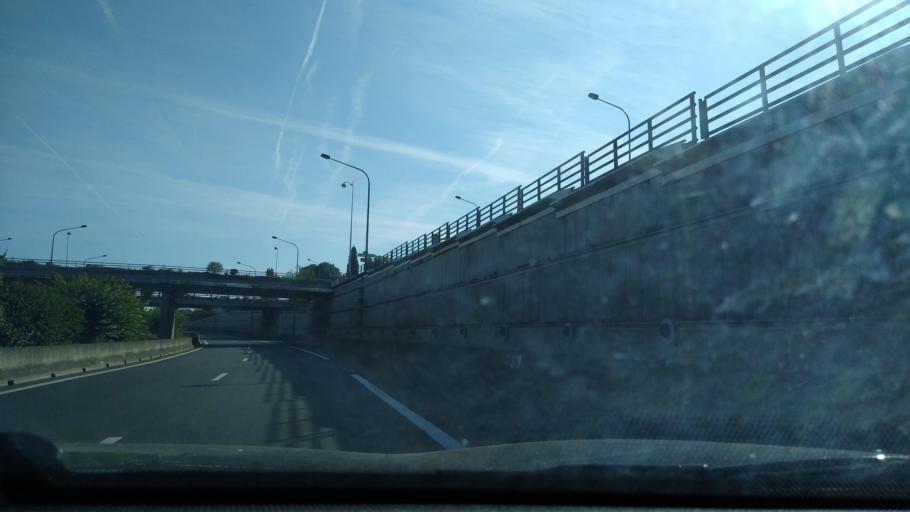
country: FR
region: Midi-Pyrenees
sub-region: Departement de la Haute-Garonne
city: Colomiers
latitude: 43.5897
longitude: 1.3605
